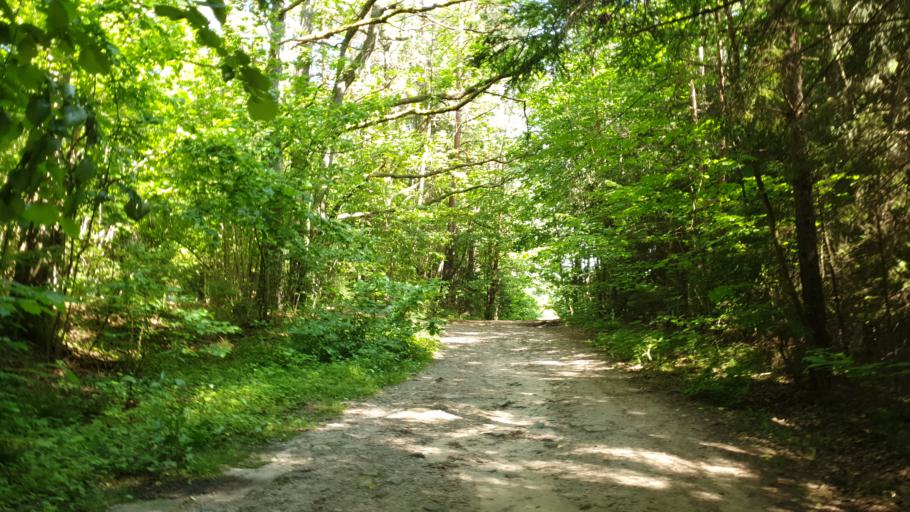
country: LT
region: Vilnius County
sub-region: Vilnius
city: Fabijoniskes
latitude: 54.7887
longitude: 25.3146
